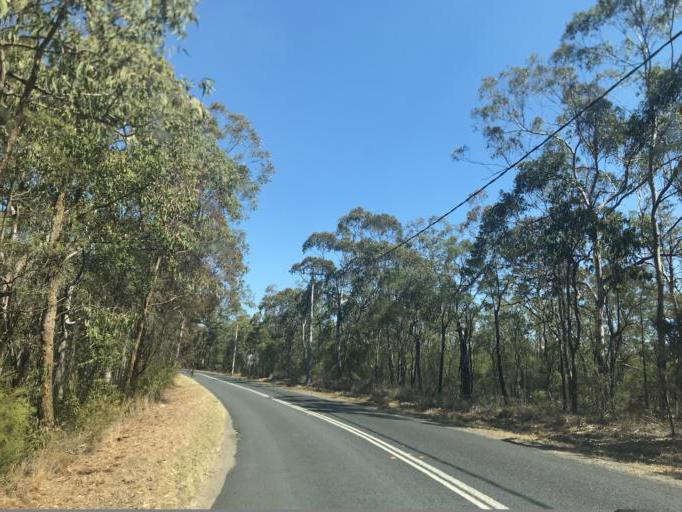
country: AU
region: New South Wales
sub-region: Hawkesbury
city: Pitt Town
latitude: -33.4513
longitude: 150.8655
